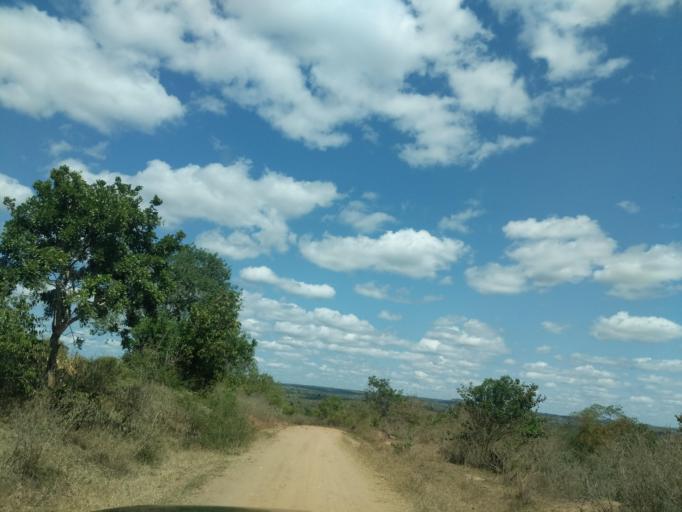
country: TZ
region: Tanga
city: Chanika
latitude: -5.5057
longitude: 38.3674
